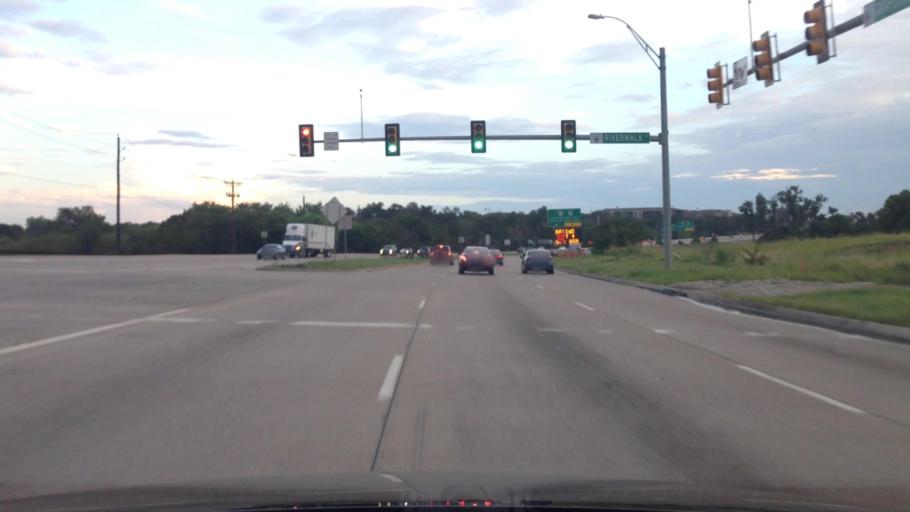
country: US
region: Texas
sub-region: Dallas County
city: Coppell
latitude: 32.9831
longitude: -97.0390
